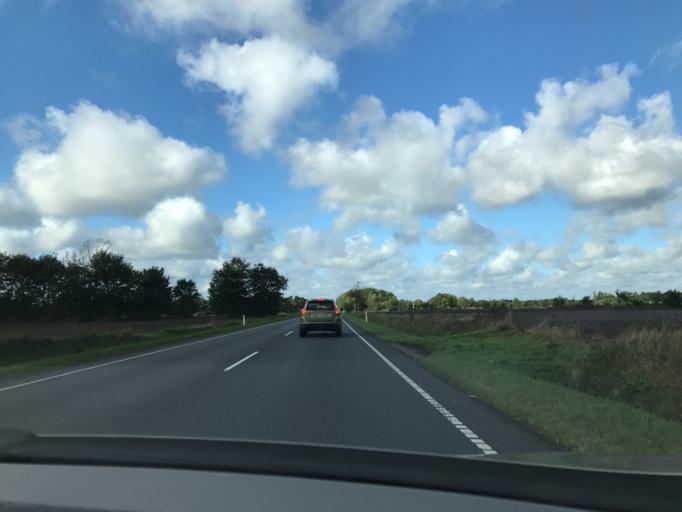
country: DK
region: South Denmark
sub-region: Billund Kommune
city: Billund
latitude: 55.7216
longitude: 9.1546
